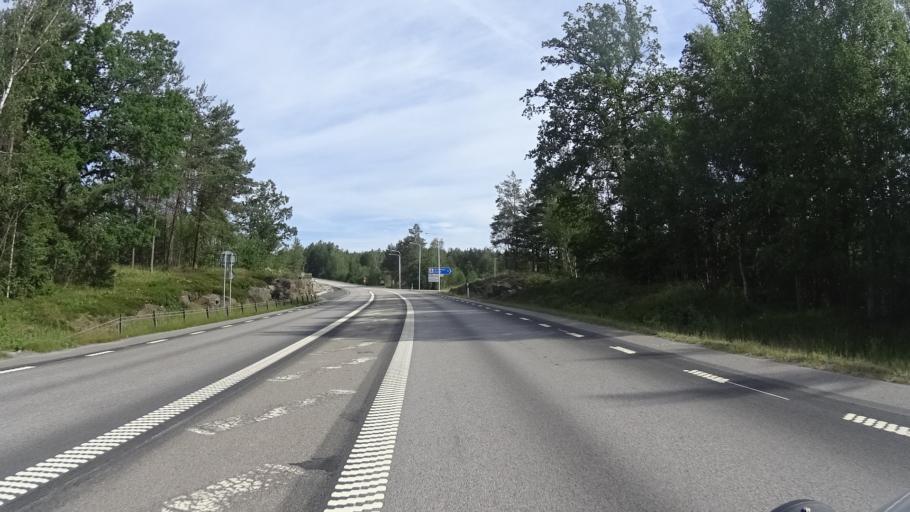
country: SE
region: Kalmar
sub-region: Vasterviks Kommun
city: Ankarsrum
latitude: 57.5875
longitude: 16.4865
